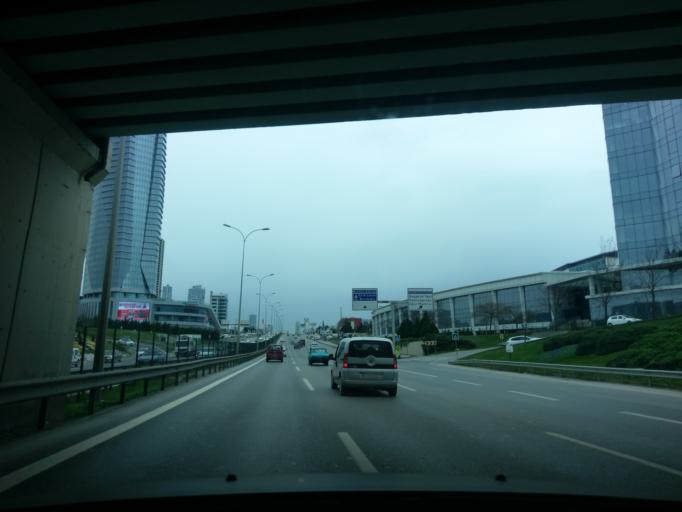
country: TR
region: Istanbul
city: Maltepe
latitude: 40.9190
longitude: 29.1712
